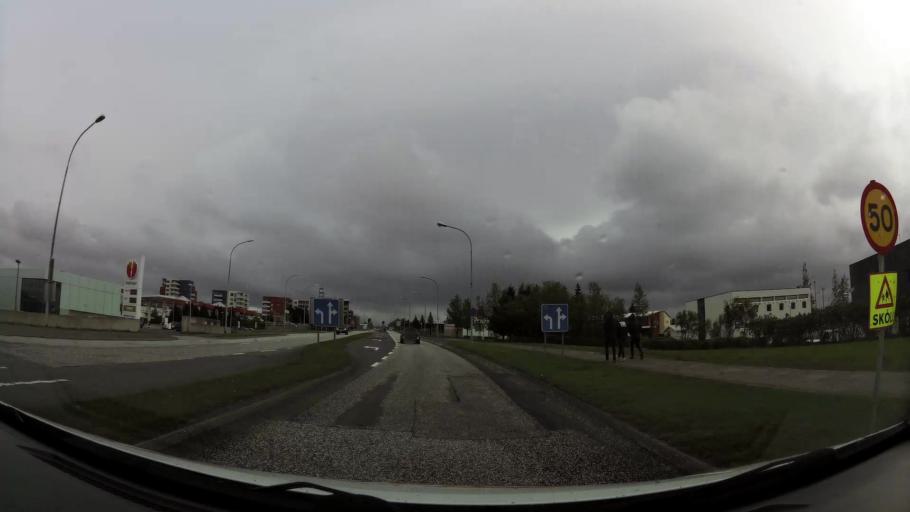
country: IS
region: Capital Region
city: Gardabaer
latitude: 64.0900
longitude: -21.9273
